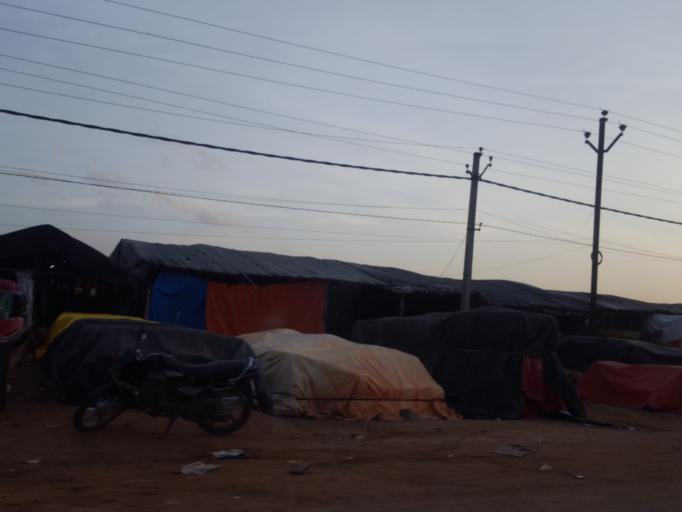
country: IN
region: Telangana
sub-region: Rangareddi
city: Kukatpalli
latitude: 17.5410
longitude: 78.3915
